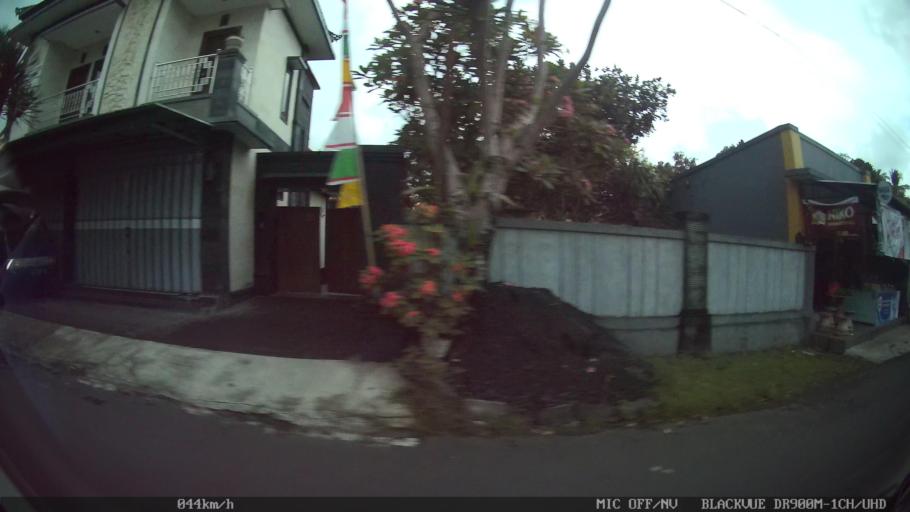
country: ID
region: Bali
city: Banjar Cemenggon
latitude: -8.5366
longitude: 115.1918
